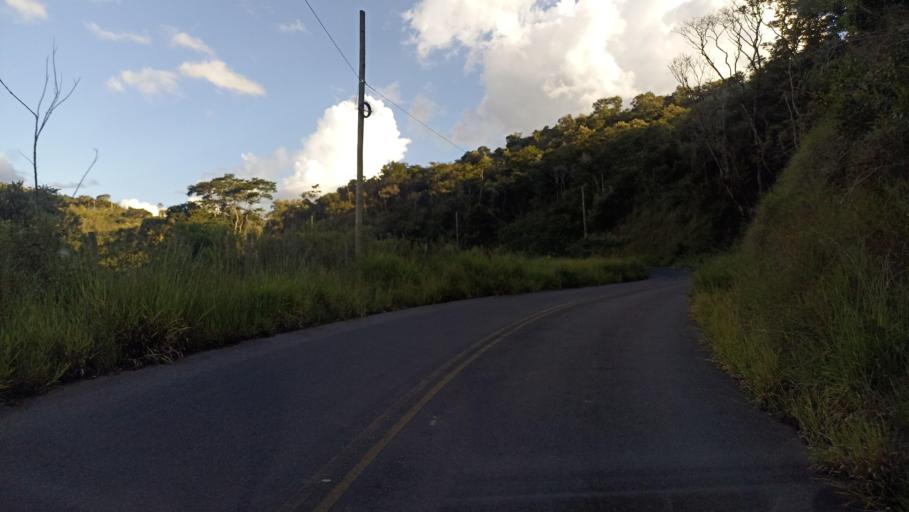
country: BR
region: Minas Gerais
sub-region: Ouro Preto
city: Ouro Preto
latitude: -20.3169
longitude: -43.6166
